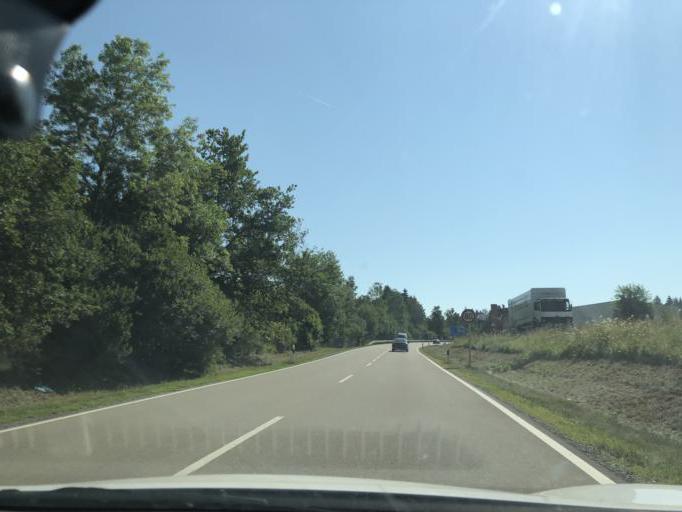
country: DE
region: Bavaria
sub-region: Swabia
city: Oy-Mittelberg
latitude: 47.6553
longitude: 10.4613
